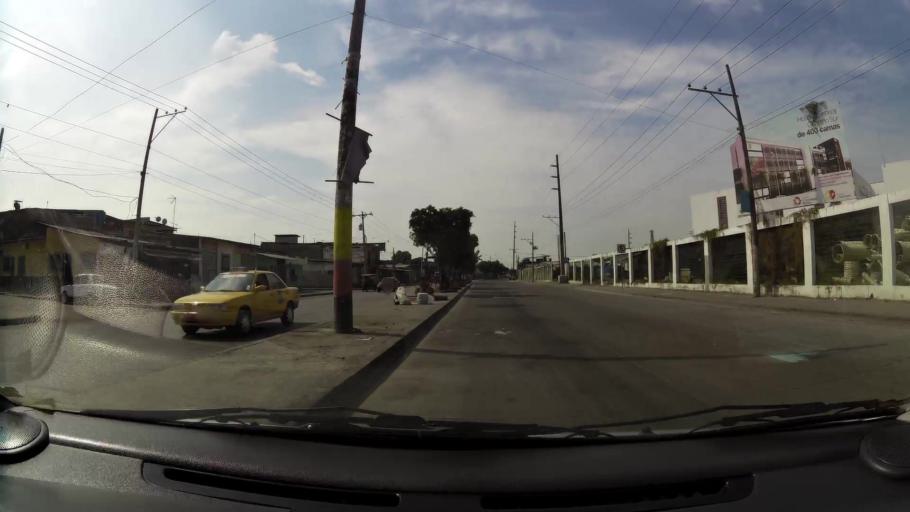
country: EC
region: Guayas
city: Guayaquil
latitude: -2.2752
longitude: -79.8954
